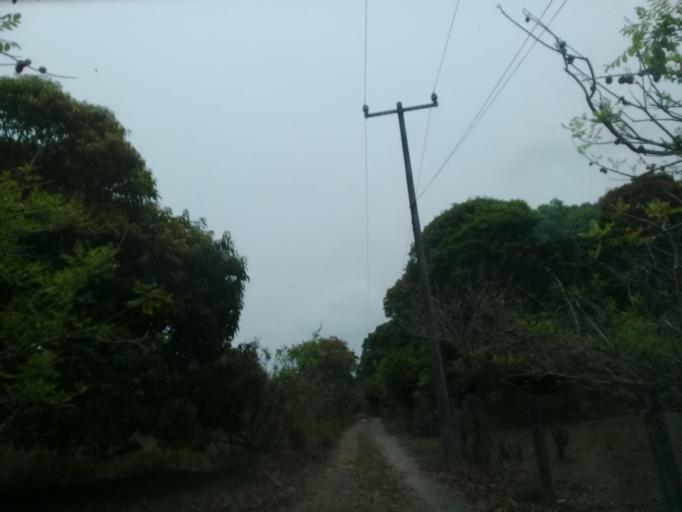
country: MX
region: Veracruz
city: Jamapa
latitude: 19.0418
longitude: -96.1976
